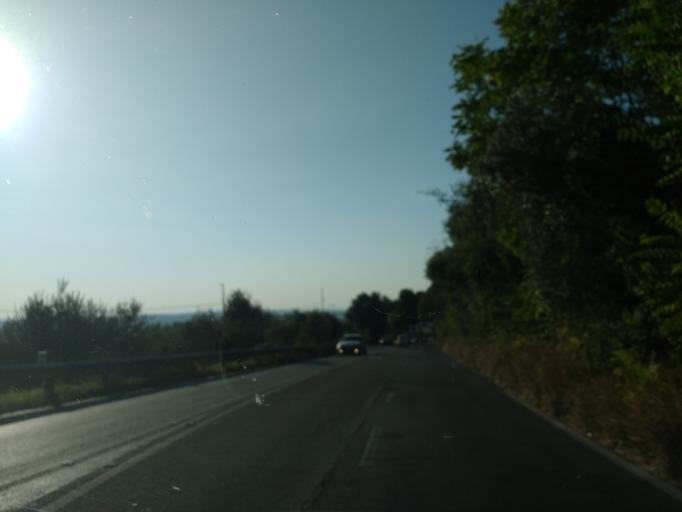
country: IT
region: Latium
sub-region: Citta metropolitana di Roma Capitale
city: Tivoli
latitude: 41.9489
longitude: 12.7902
